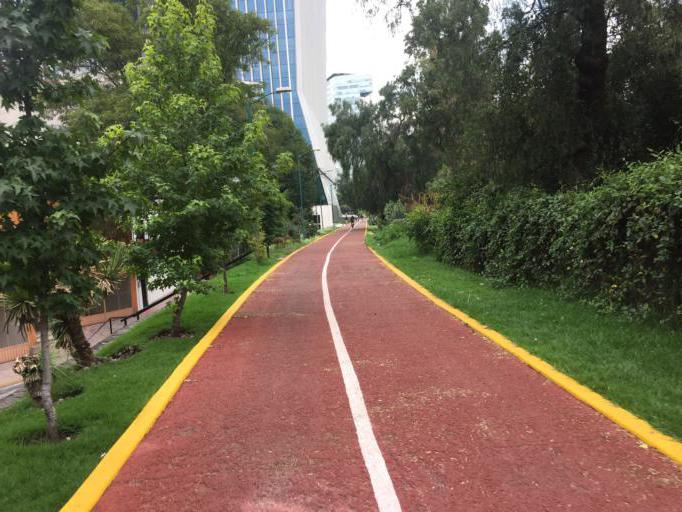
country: MX
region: Mexico City
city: Polanco
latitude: 19.4238
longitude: -99.2026
